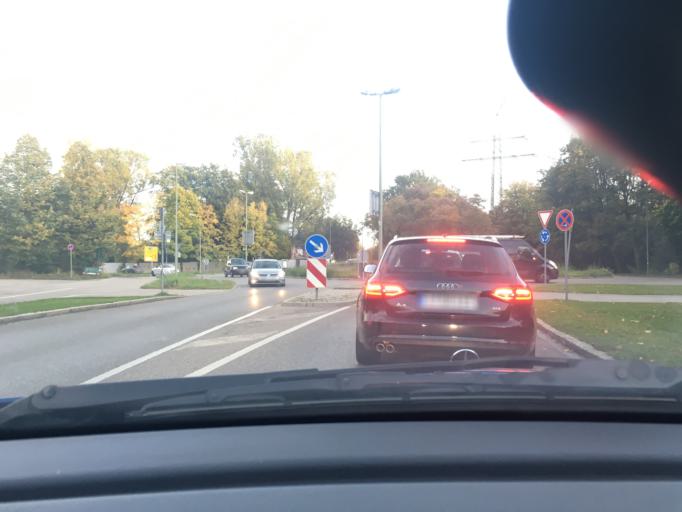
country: DE
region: Bavaria
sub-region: Swabia
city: Stadtbergen
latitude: 48.3868
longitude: 10.8420
